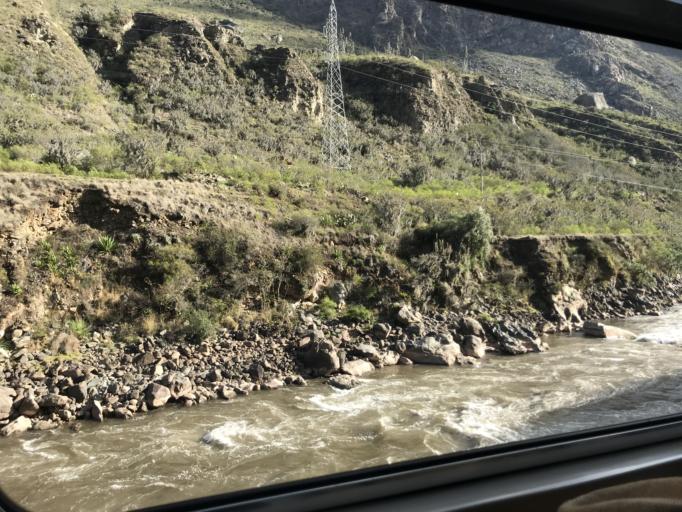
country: PE
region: Cusco
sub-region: Provincia de Urubamba
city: Ollantaytambo
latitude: -13.2247
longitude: -72.3976
